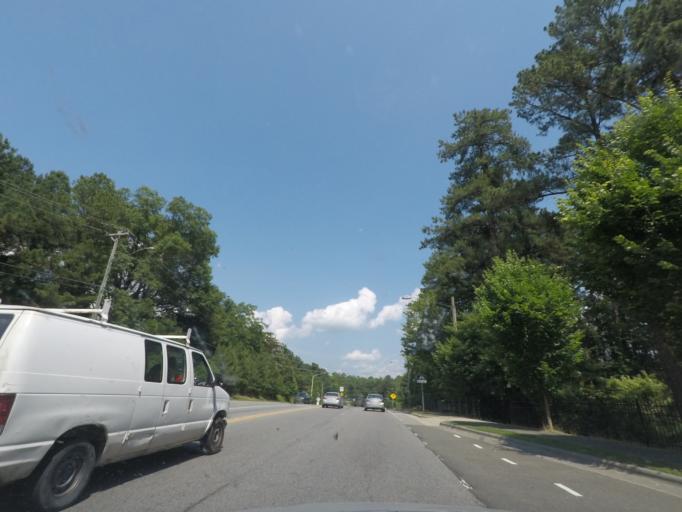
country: US
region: North Carolina
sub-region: Durham County
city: Durham
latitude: 35.9583
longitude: -78.9475
